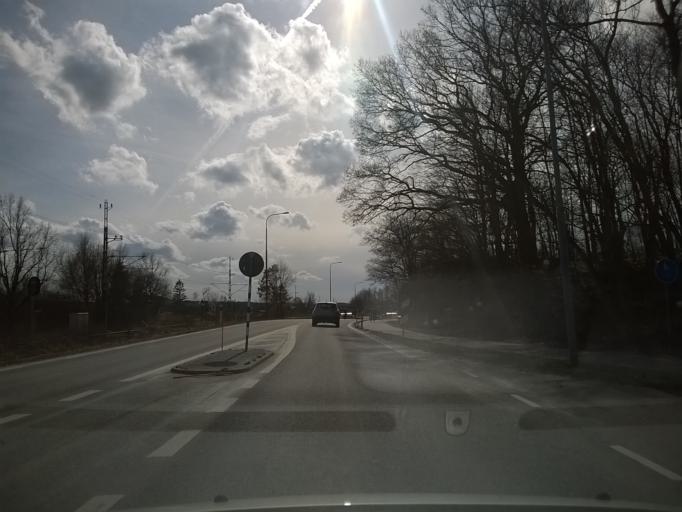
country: SE
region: Vaestra Goetaland
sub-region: Stenungsunds Kommun
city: Stora Hoga
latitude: 58.0212
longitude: 11.8367
